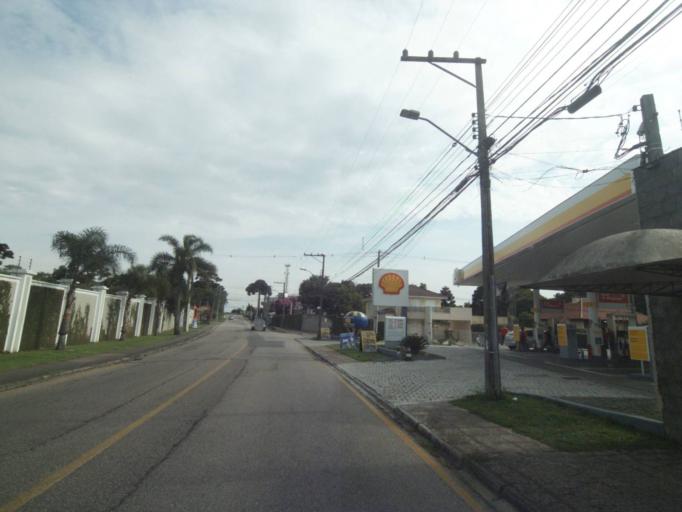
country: BR
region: Parana
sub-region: Curitiba
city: Curitiba
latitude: -25.4049
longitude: -49.3137
